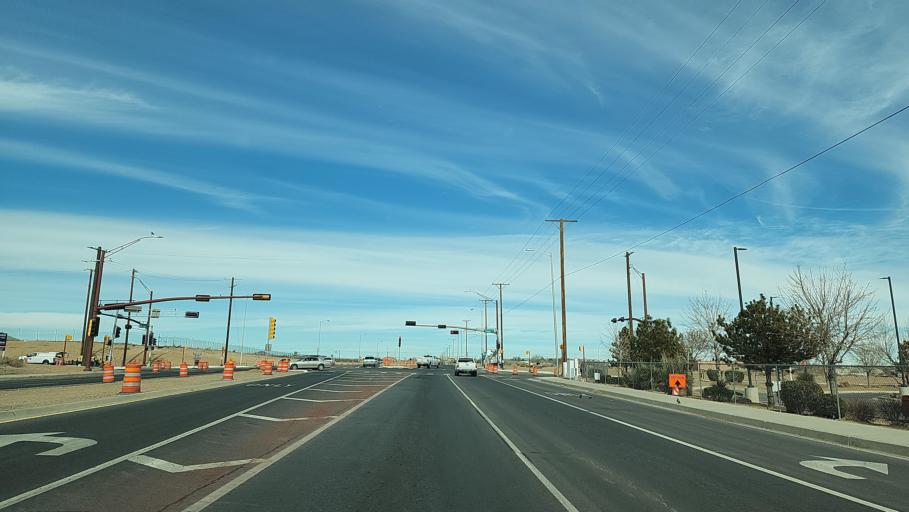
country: US
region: New Mexico
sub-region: Bernalillo County
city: Albuquerque
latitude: 35.0655
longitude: -106.7099
